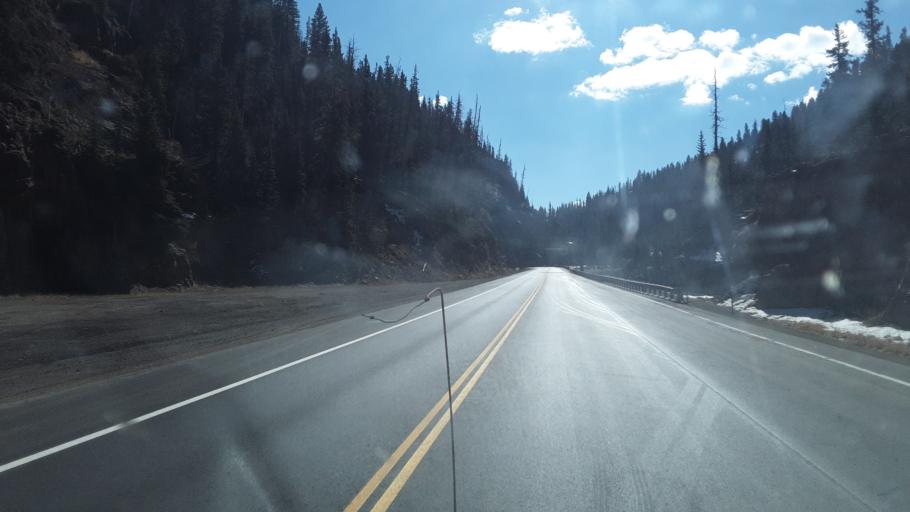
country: US
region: Colorado
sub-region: Mineral County
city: Creede
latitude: 37.5522
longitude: -106.7765
